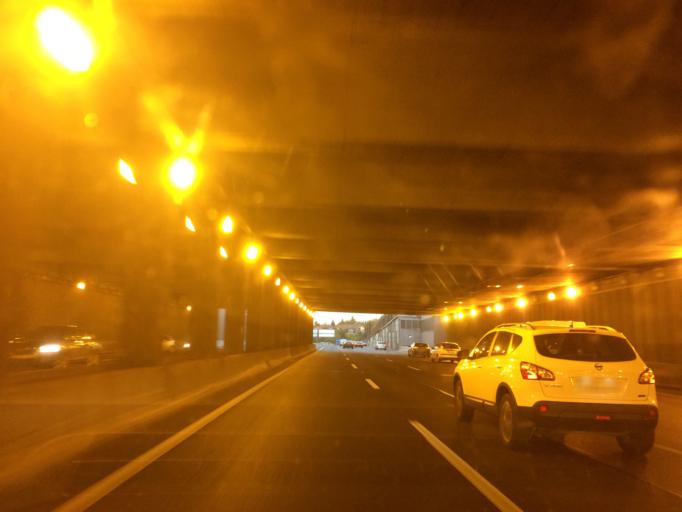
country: ES
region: Madrid
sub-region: Provincia de Madrid
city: Tetuan de las Victorias
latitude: 40.4728
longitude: -3.7349
